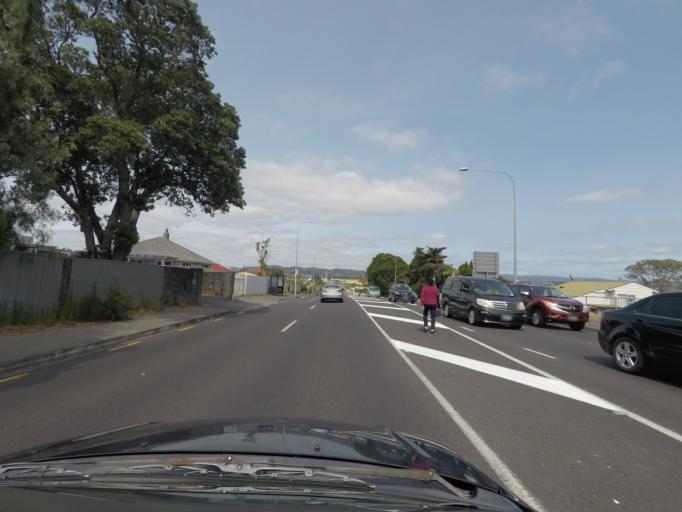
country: NZ
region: Auckland
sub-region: Auckland
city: Rosebank
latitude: -36.9063
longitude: 174.7012
